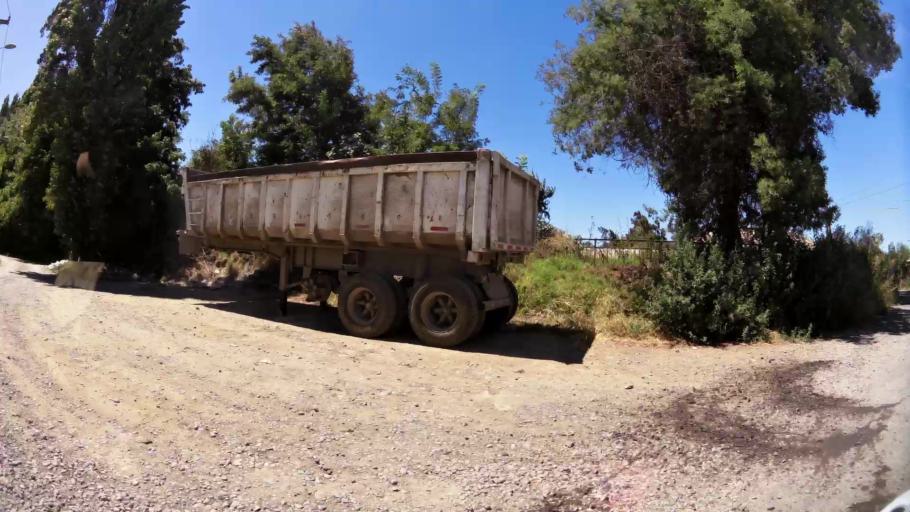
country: CL
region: O'Higgins
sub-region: Provincia de Cachapoal
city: Rancagua
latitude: -34.1537
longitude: -70.7494
